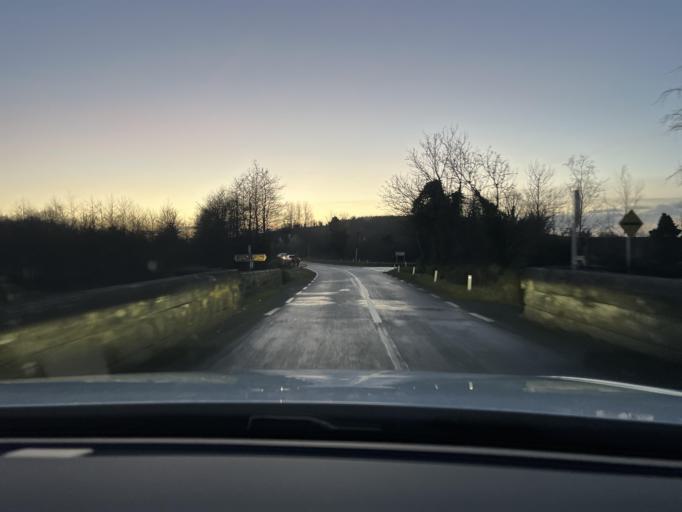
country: IE
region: Connaught
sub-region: County Leitrim
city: Carrick-on-Shannon
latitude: 54.0079
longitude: -8.0161
